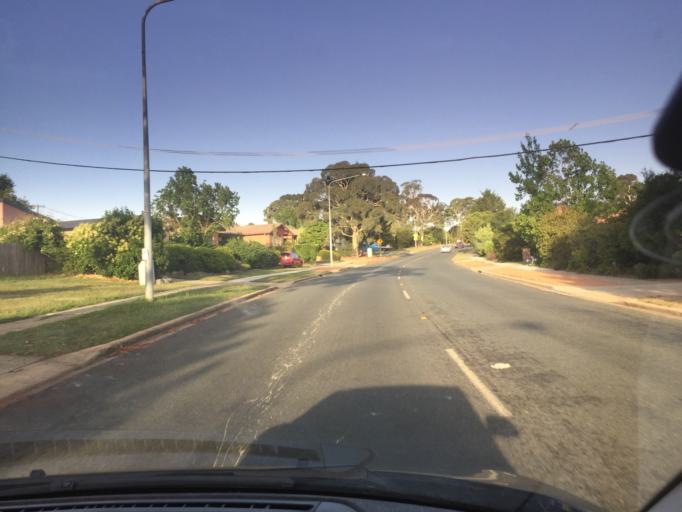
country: AU
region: Australian Capital Territory
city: Kaleen
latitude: -35.2180
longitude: 149.1061
